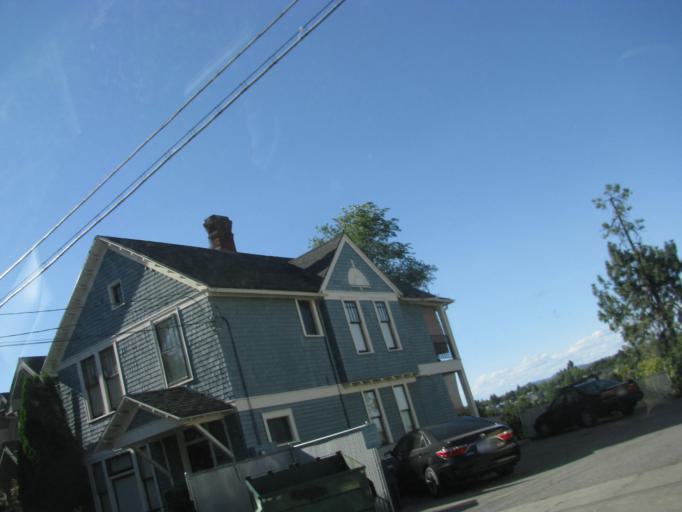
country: US
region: Washington
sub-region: Spokane County
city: Spokane
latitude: 47.6572
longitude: -117.4428
